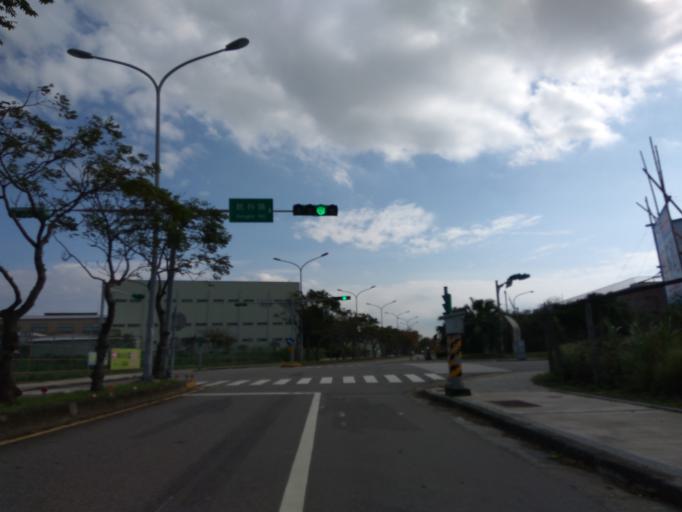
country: TW
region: Taiwan
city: Taoyuan City
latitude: 25.0587
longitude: 121.1795
